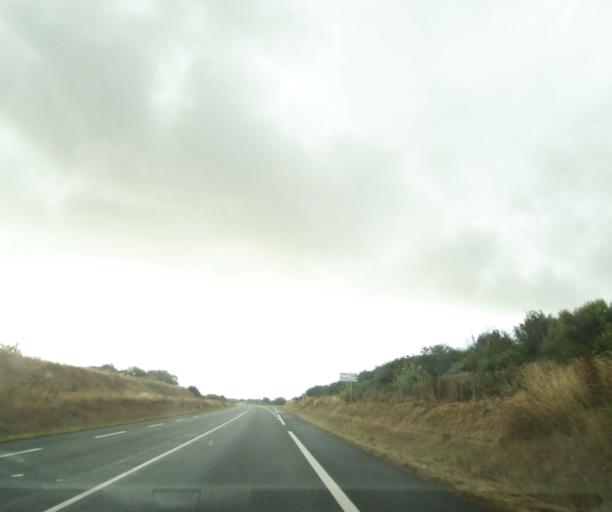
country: FR
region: Pays de la Loire
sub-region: Departement de la Vendee
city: Saint-Hilaire-de-Talmont
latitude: 46.4652
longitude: -1.6421
